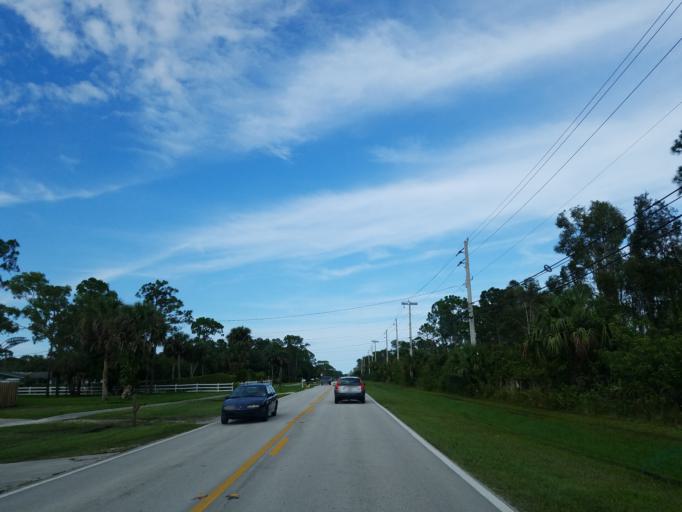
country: US
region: Florida
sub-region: Martin County
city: Palm City
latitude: 27.1250
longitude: -80.2500
